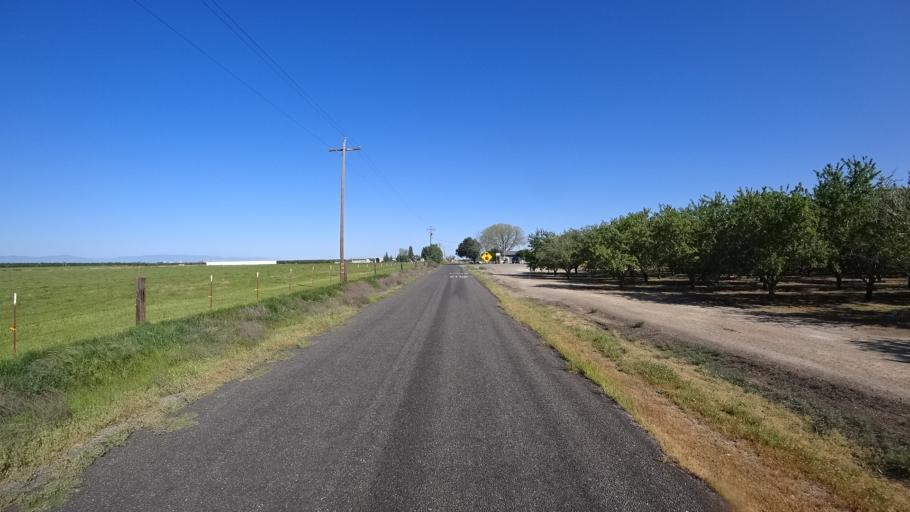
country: US
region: California
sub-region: Glenn County
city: Hamilton City
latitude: 39.7077
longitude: -122.0773
